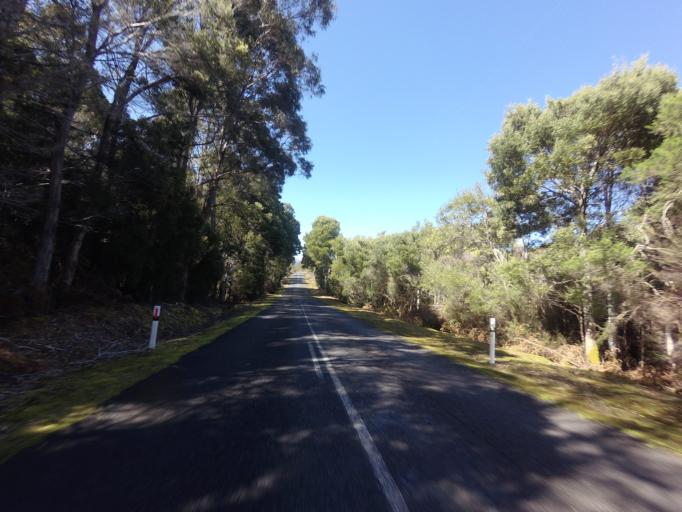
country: AU
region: Tasmania
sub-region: Derwent Valley
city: New Norfolk
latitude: -42.7597
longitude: 146.5306
